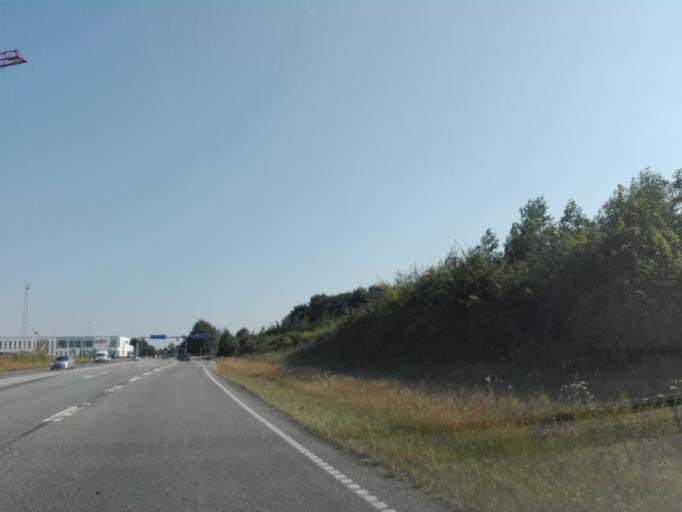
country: DK
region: Central Jutland
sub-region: Arhus Kommune
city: Stavtrup
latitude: 56.1108
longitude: 10.1169
